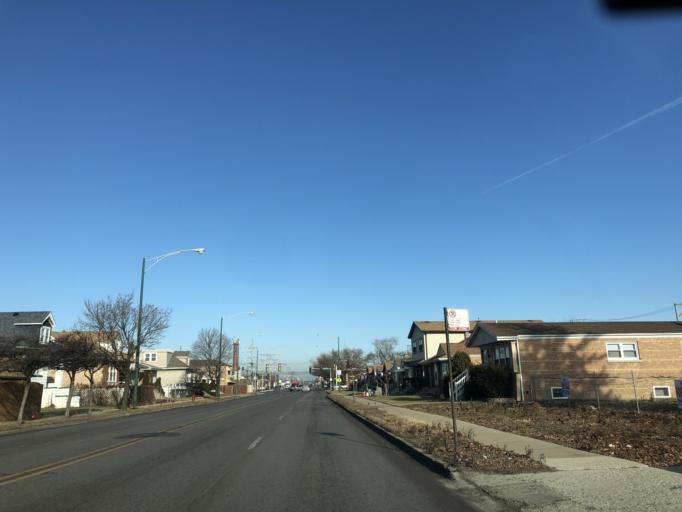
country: US
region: Illinois
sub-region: Cook County
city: Stickney
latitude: 41.7985
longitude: -87.7625
